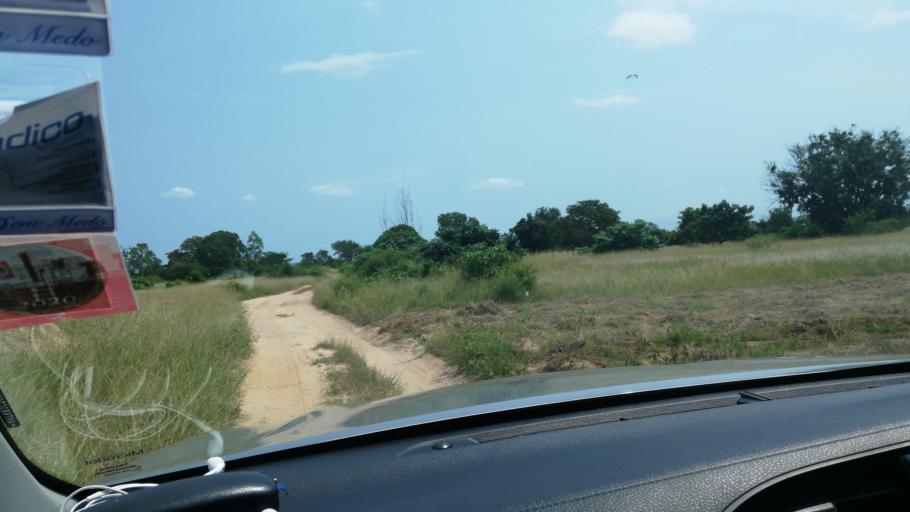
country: MZ
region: Maputo
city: Matola
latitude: -26.1101
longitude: 32.4166
